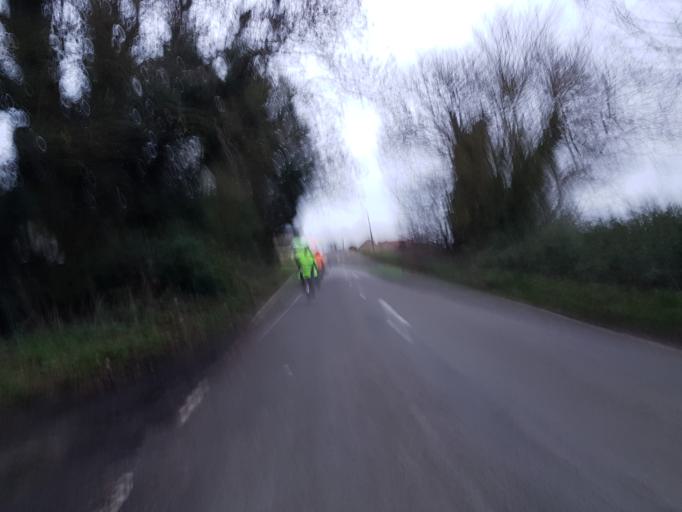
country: GB
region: England
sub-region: Cambridgeshire
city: Waterbeach
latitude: 52.2185
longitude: 0.1806
